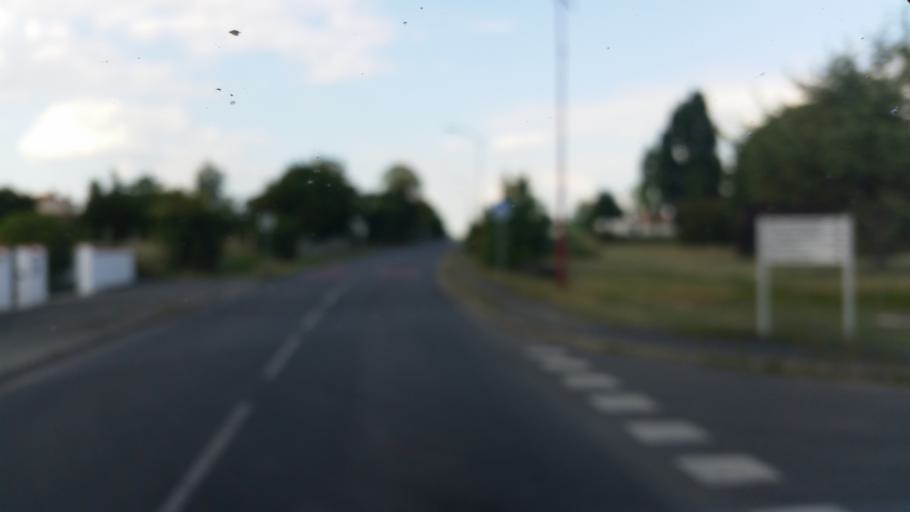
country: FR
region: Poitou-Charentes
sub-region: Departement de la Charente-Maritime
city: Andilly
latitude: 46.2553
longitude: -1.0220
